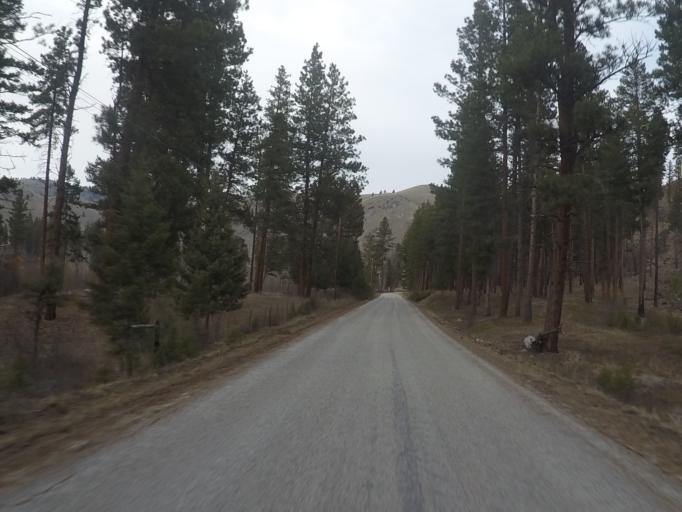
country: US
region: Montana
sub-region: Ravalli County
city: Hamilton
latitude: 45.8518
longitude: -114.0316
